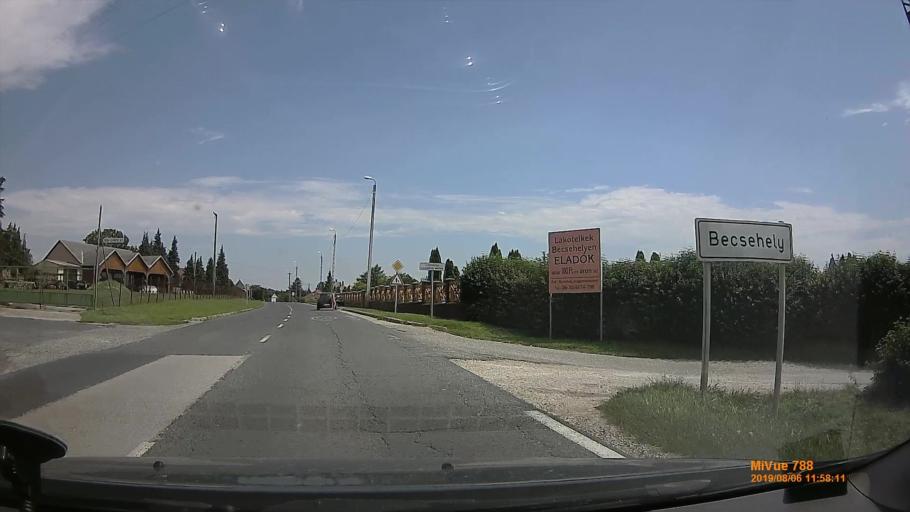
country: HU
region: Zala
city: Becsehely
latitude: 46.4436
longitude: 16.7667
